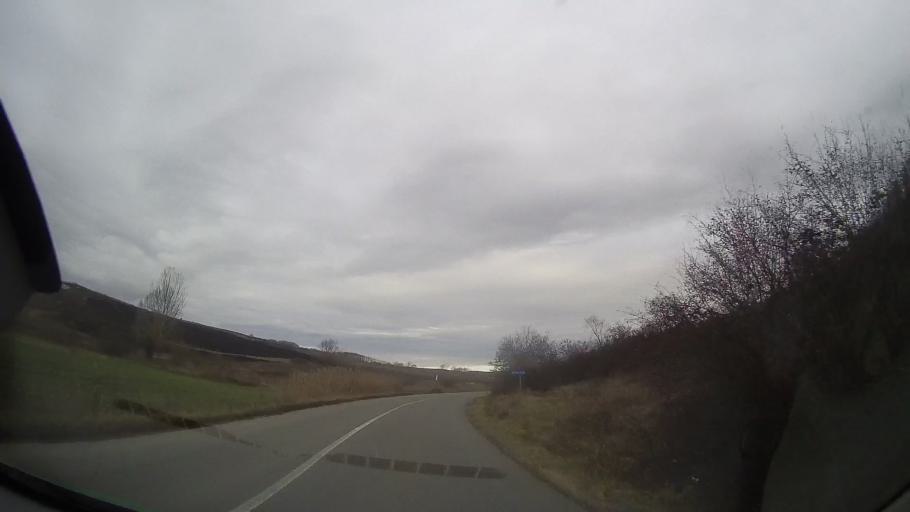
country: RO
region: Mures
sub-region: Comuna Bala
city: Bala
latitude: 46.7272
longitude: 24.5432
